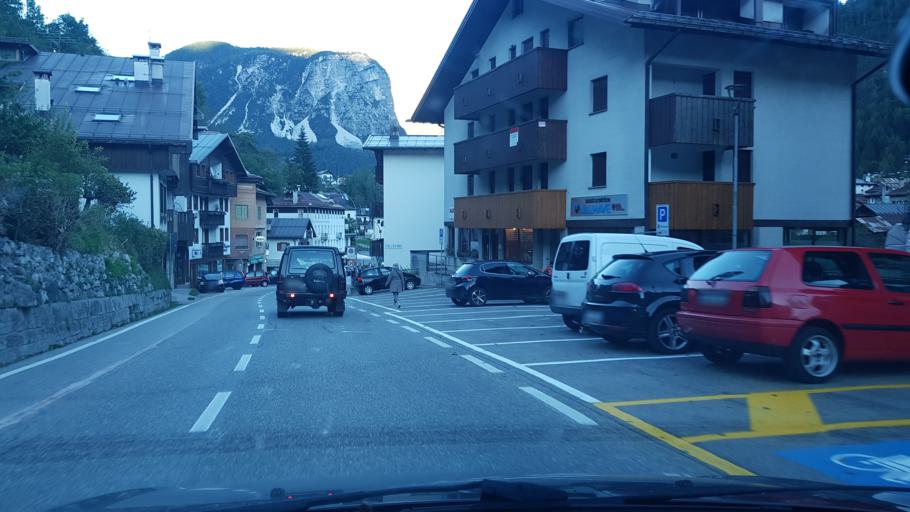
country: IT
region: Veneto
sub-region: Provincia di Belluno
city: Forno di Zoldo
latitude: 46.3460
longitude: 12.1743
